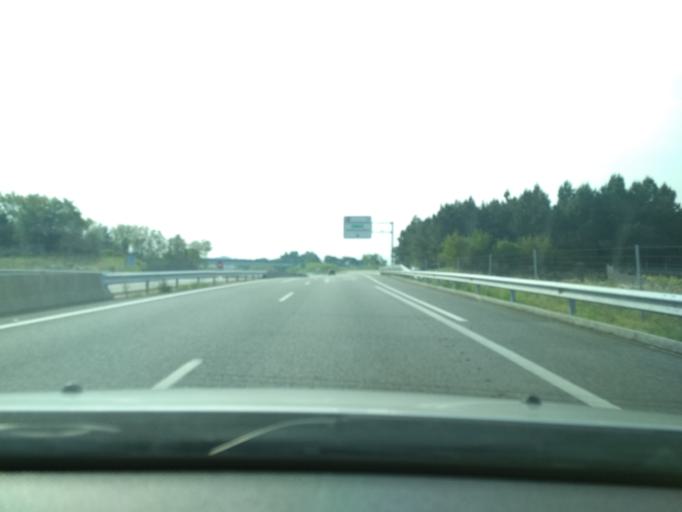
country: ES
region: Galicia
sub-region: Provincia da Coruna
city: Rianxo
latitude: 42.6720
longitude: -8.8295
